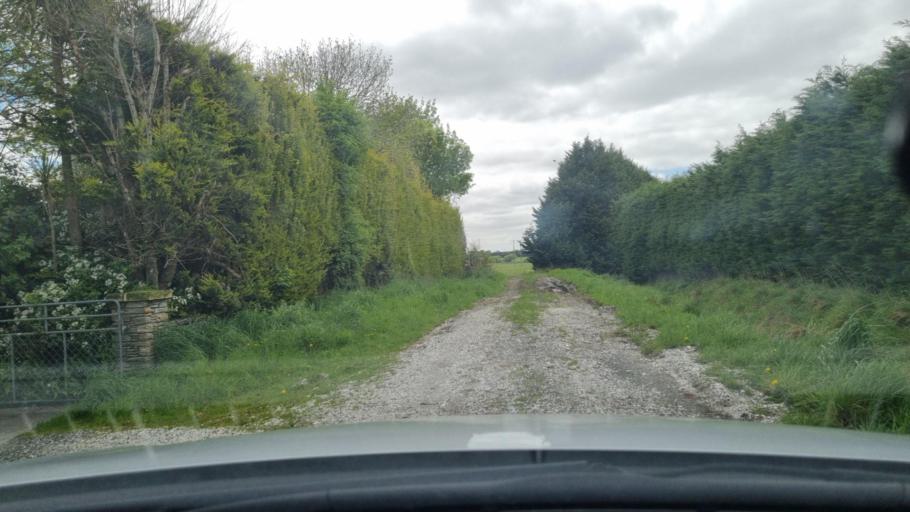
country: NZ
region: Southland
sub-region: Invercargill City
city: Invercargill
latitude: -46.3891
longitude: 168.4041
